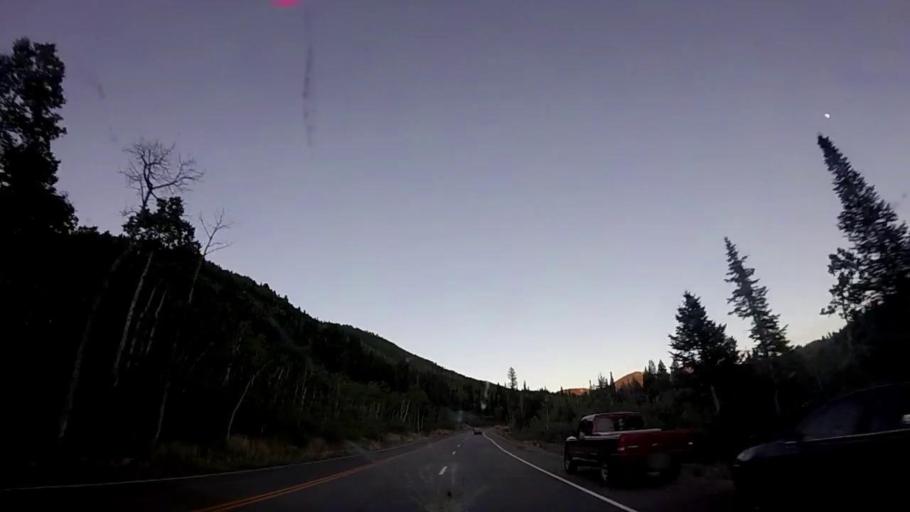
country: US
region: Utah
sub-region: Summit County
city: Snyderville
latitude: 40.6299
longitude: -111.6032
